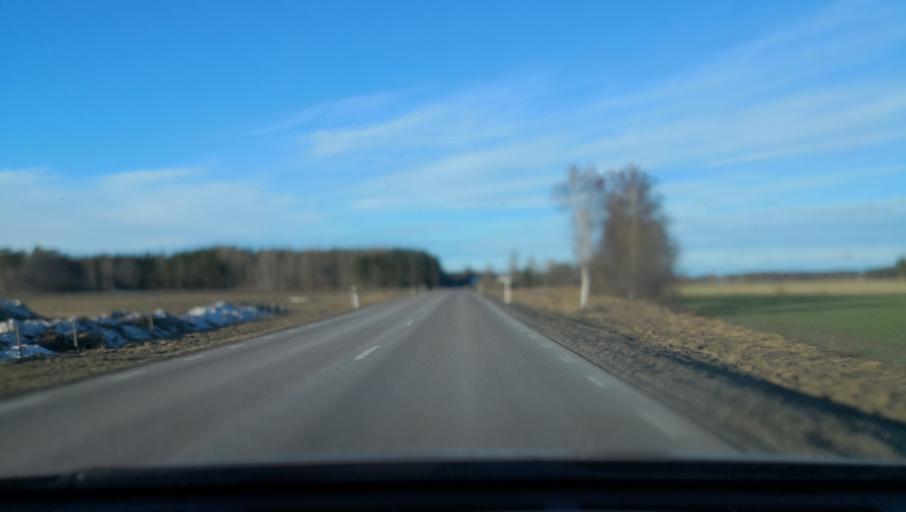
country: SE
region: Uppsala
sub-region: Osthammars Kommun
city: Gimo
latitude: 60.1825
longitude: 18.1904
